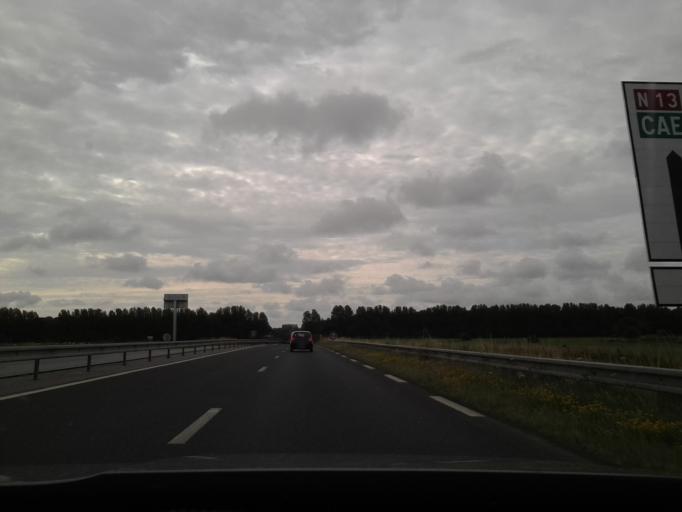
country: FR
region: Lower Normandy
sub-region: Departement de la Manche
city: Carentan
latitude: 49.3172
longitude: -1.2362
